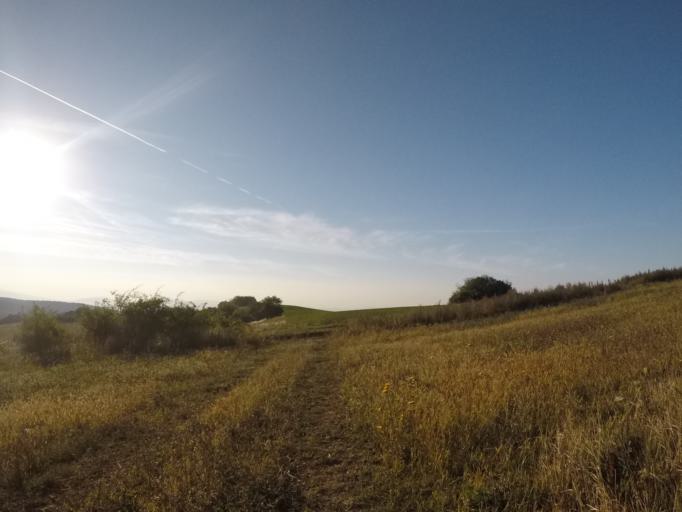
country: SK
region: Kosicky
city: Kosice
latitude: 48.7511
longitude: 21.1290
